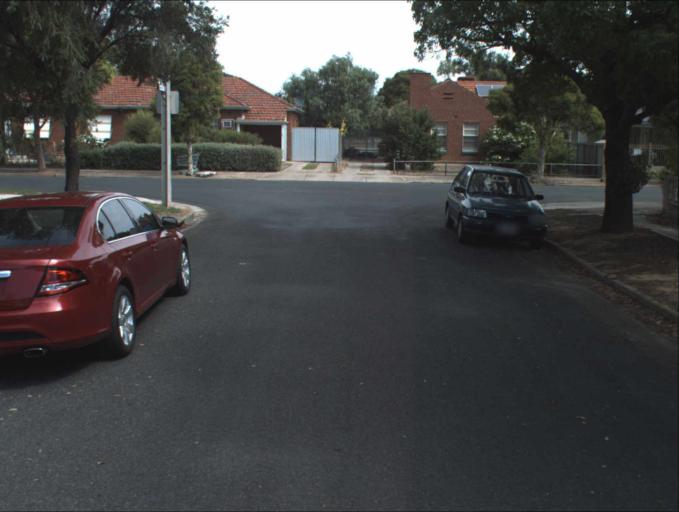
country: AU
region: South Australia
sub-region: Port Adelaide Enfield
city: Blair Athol
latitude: -34.8579
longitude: 138.5816
